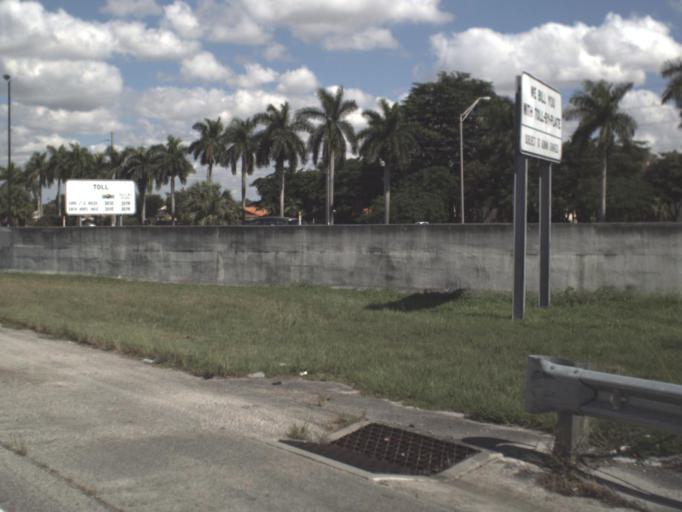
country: US
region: Florida
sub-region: Miami-Dade County
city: Westwood Lake
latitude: 25.7351
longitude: -80.3842
